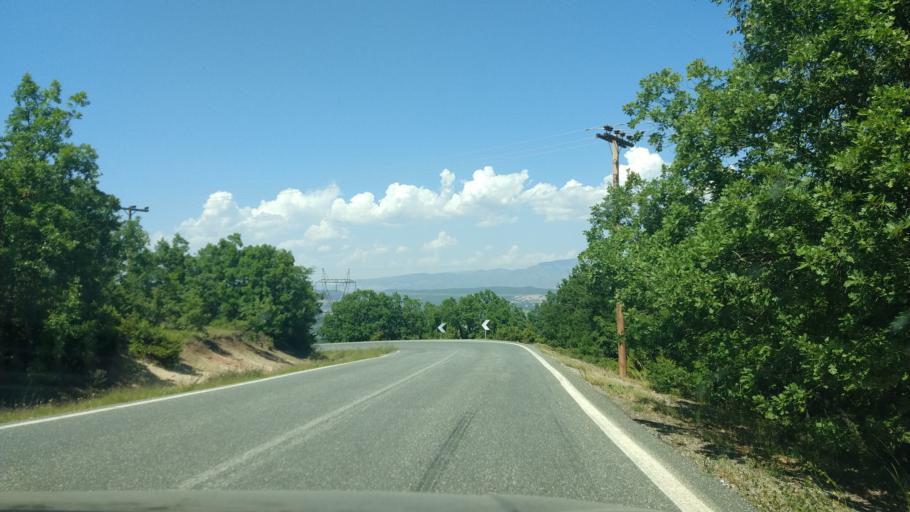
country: GR
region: West Macedonia
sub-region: Nomos Grevenon
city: Grevena
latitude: 40.0195
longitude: 21.4872
